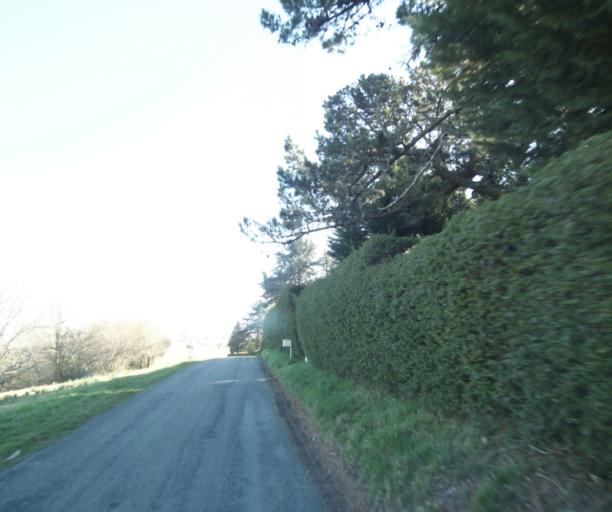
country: FR
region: Aquitaine
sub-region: Departement des Pyrenees-Atlantiques
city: Urrugne
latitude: 43.3673
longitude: -1.7356
